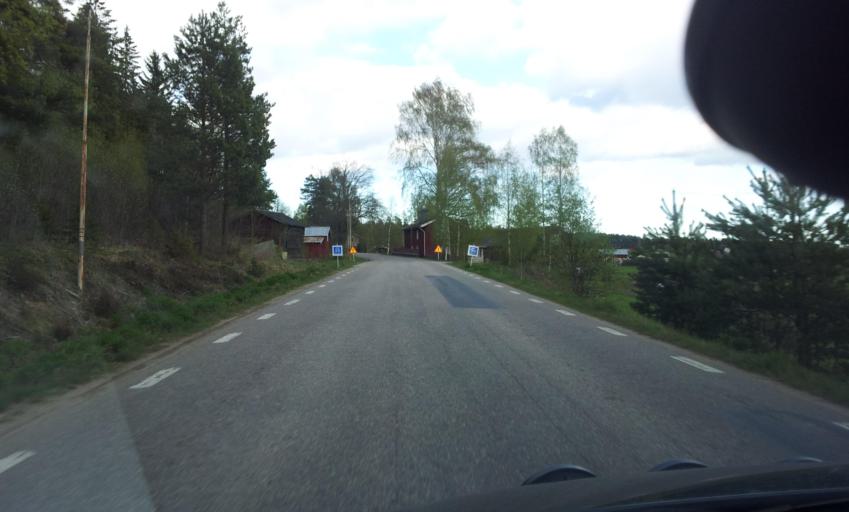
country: SE
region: Gaevleborg
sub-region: Bollnas Kommun
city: Kilafors
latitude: 61.3661
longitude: 16.6320
